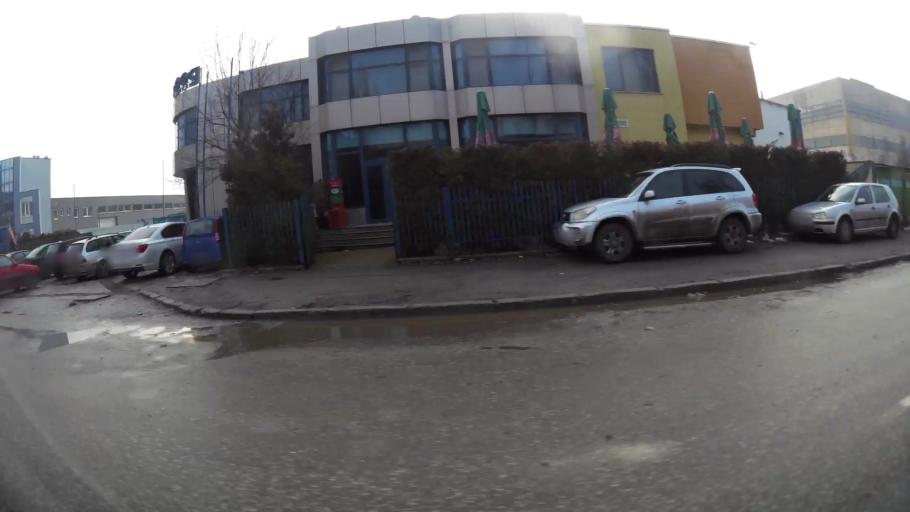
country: BG
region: Sofia-Capital
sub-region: Stolichna Obshtina
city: Sofia
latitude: 42.7369
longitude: 23.3253
